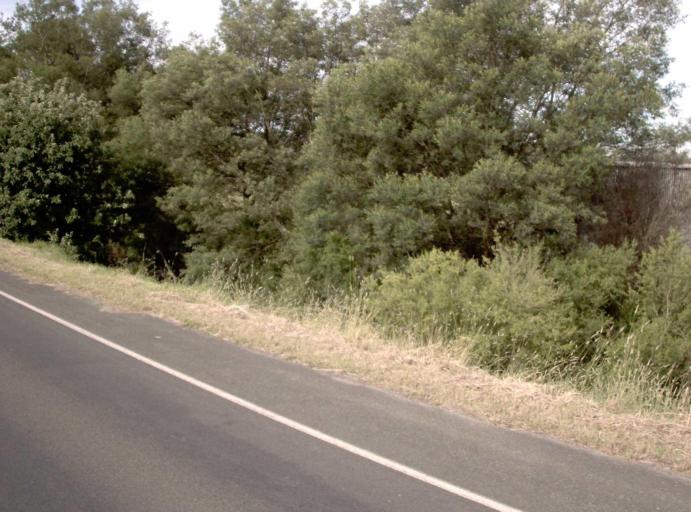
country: AU
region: Victoria
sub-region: Latrobe
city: Traralgon
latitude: -38.1542
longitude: 146.5538
